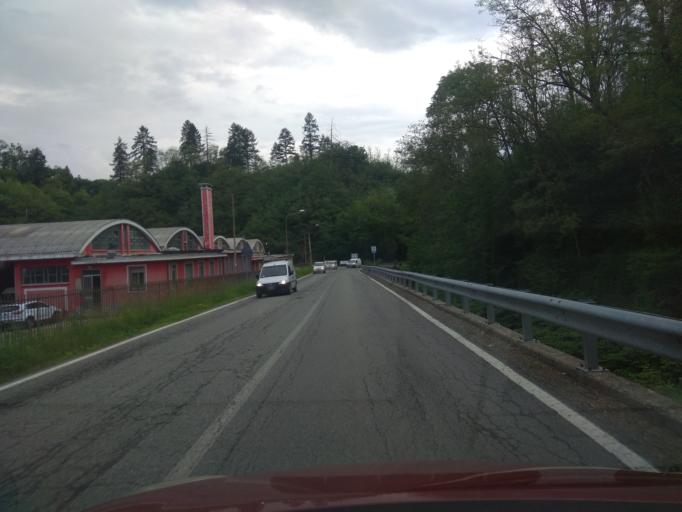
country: IT
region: Piedmont
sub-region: Provincia di Biella
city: Lanvario
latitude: 45.6580
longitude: 8.1991
